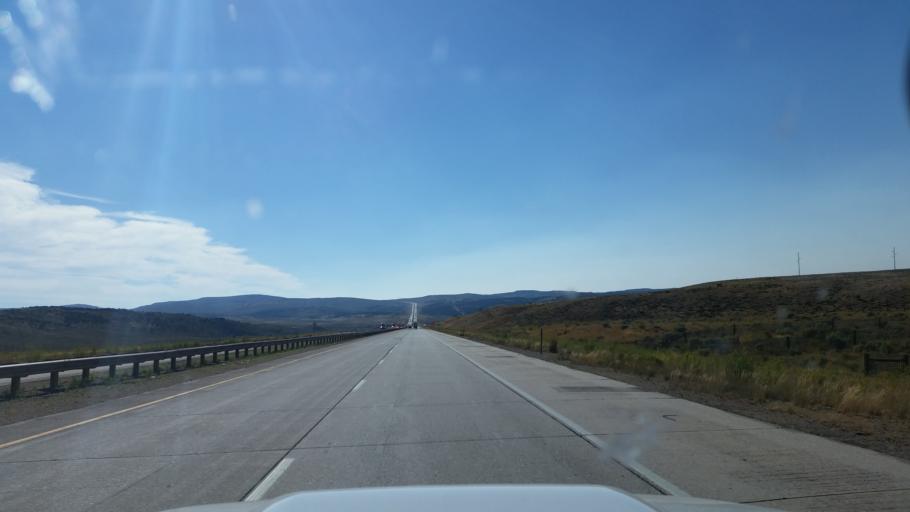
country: US
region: Wyoming
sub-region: Uinta County
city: Mountain View
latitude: 41.2982
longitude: -110.6034
